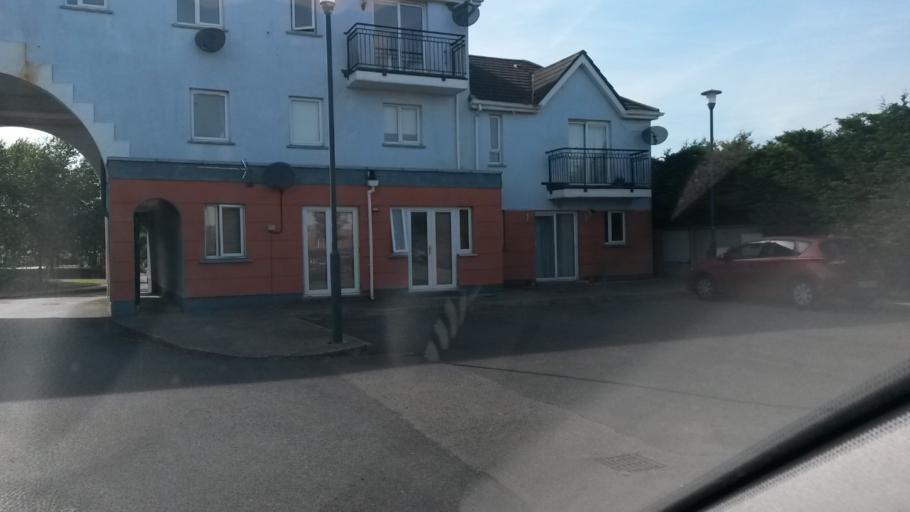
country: IE
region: Leinster
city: Lusk
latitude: 53.5226
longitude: -6.1670
